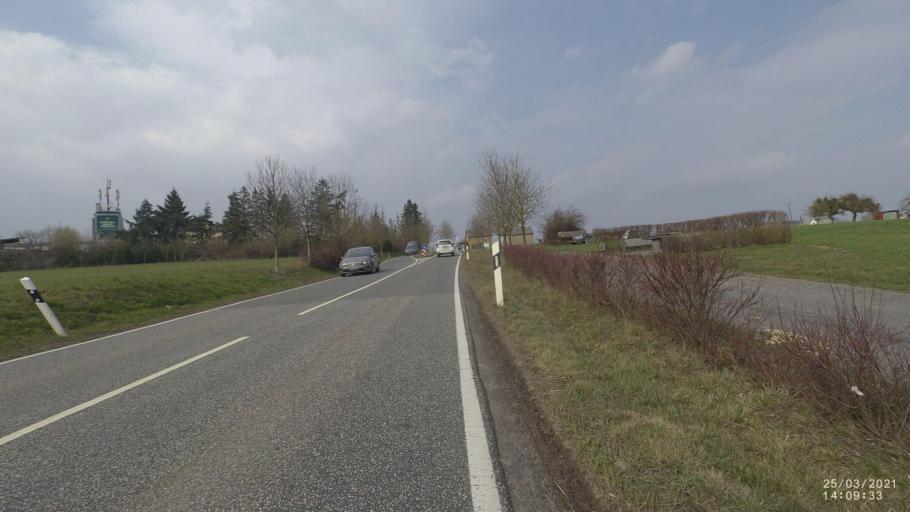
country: DE
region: Rheinland-Pfalz
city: Ettringen
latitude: 50.3494
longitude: 7.2226
